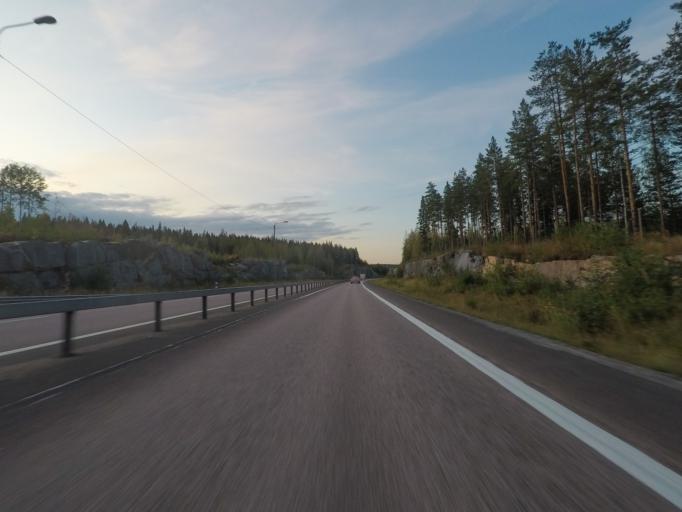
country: FI
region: Central Finland
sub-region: Jyvaeskylae
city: Saeynaetsalo
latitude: 62.2125
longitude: 25.8899
